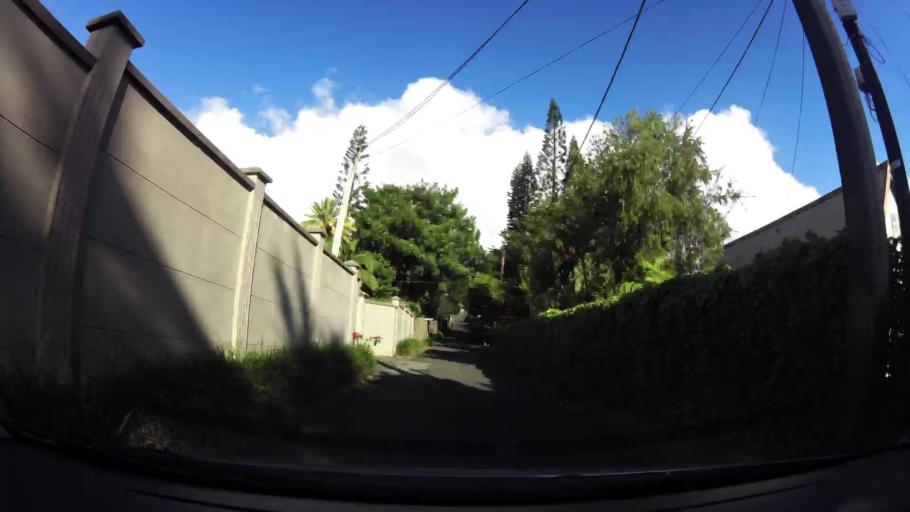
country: MU
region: Plaines Wilhems
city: Curepipe
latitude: -20.3124
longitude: 57.5025
